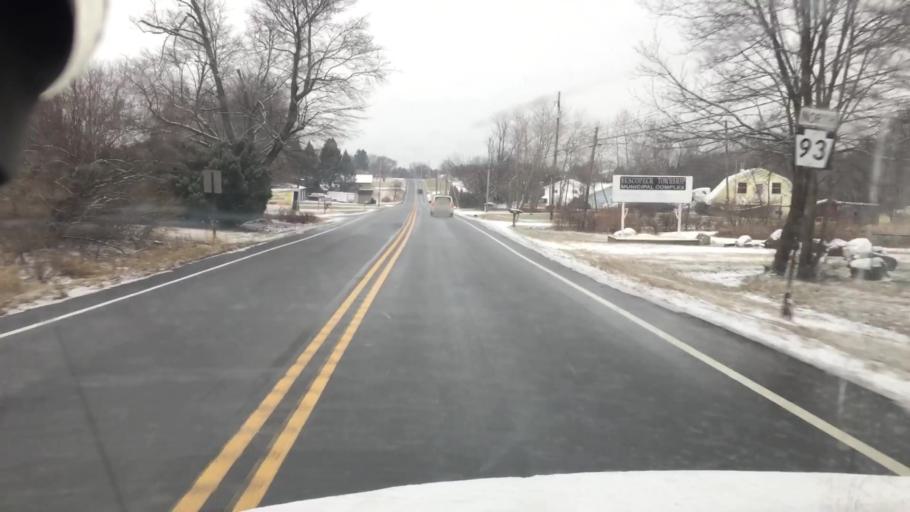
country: US
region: Pennsylvania
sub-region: Luzerne County
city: Nescopeck
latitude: 41.0439
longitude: -76.1440
